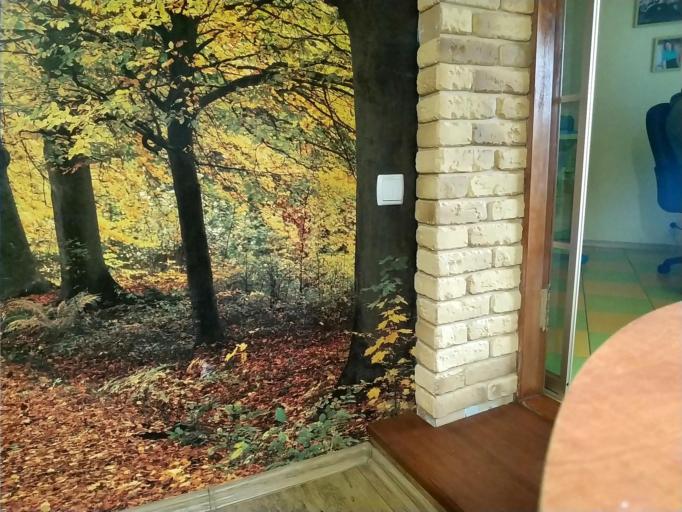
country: RU
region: Smolensk
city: Dorogobuzh
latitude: 54.9758
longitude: 33.2760
